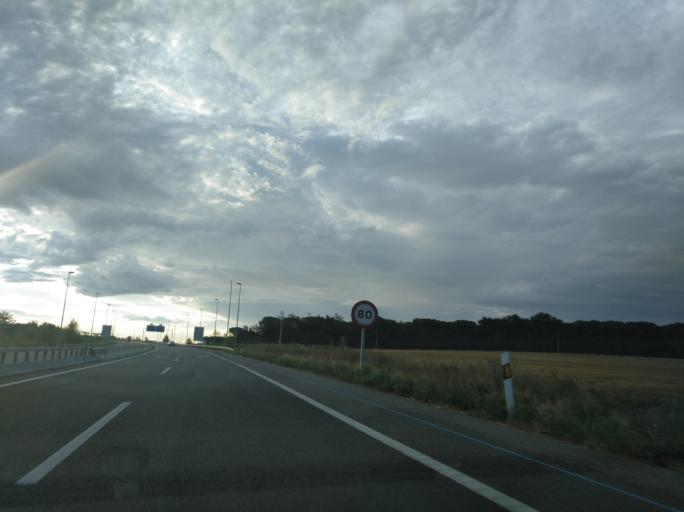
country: ES
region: Catalonia
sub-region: Provincia de Girona
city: Vilobi d'Onyar
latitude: 41.8689
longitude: 2.7699
